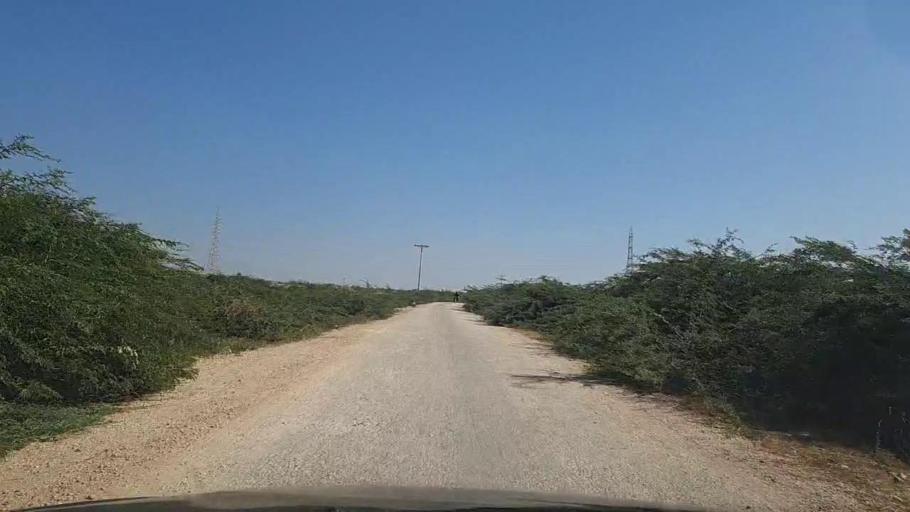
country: PK
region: Sindh
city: Thatta
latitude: 24.6296
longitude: 67.8311
